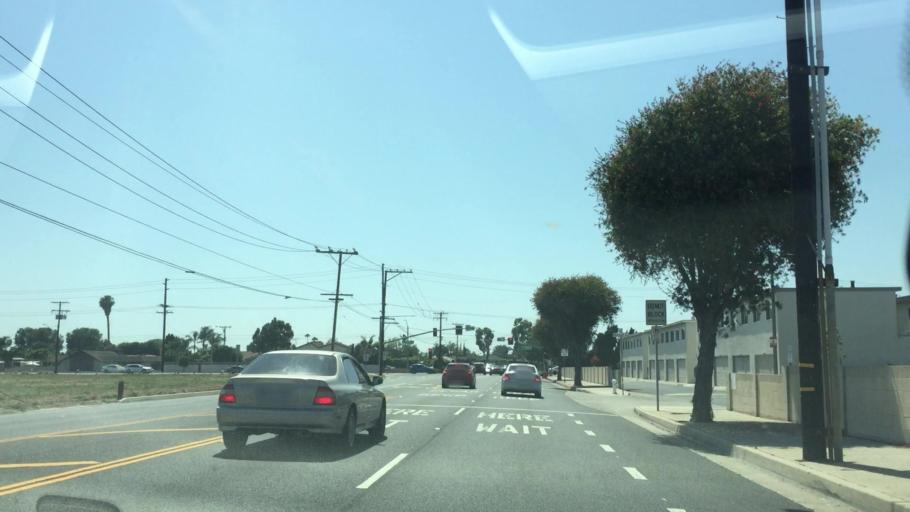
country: US
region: California
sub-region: Orange County
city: Fountain Valley
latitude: 33.7092
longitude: -117.9353
